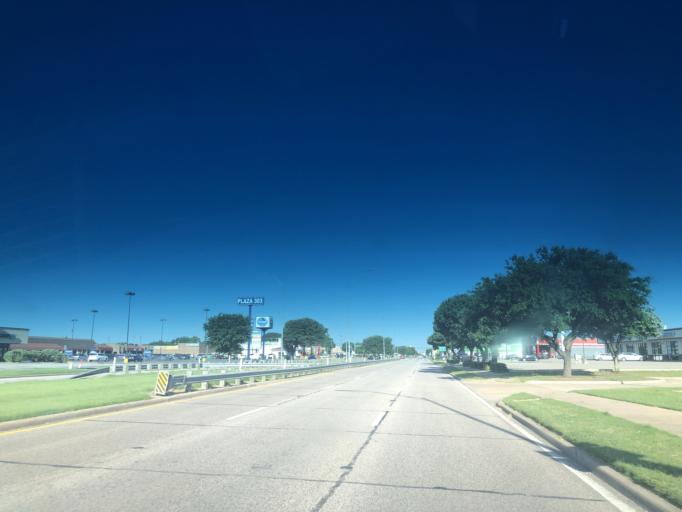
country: US
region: Texas
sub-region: Dallas County
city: Grand Prairie
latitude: 32.7096
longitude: -96.9995
